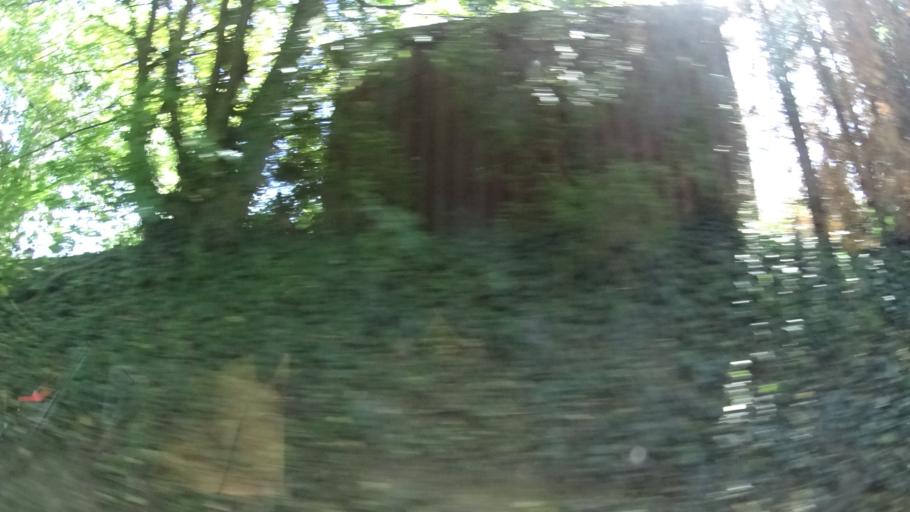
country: DE
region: Baden-Wuerttemberg
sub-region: Karlsruhe Region
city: Ubstadt-Weiher
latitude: 49.1309
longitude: 8.6518
